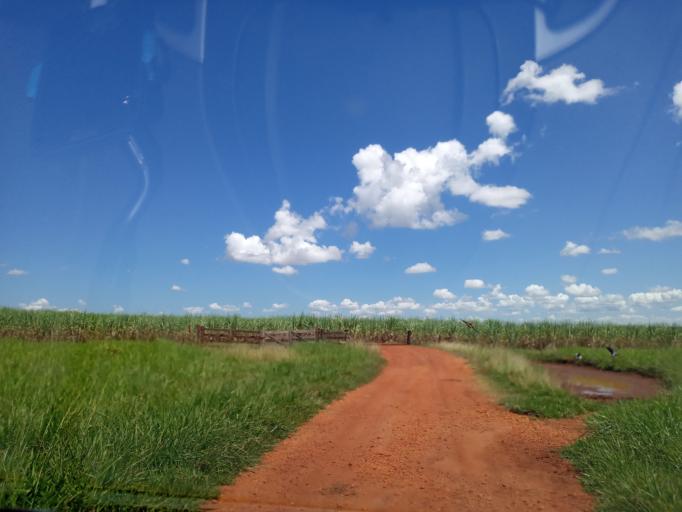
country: BR
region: Goias
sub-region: Itumbiara
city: Itumbiara
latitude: -18.3989
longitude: -49.1306
